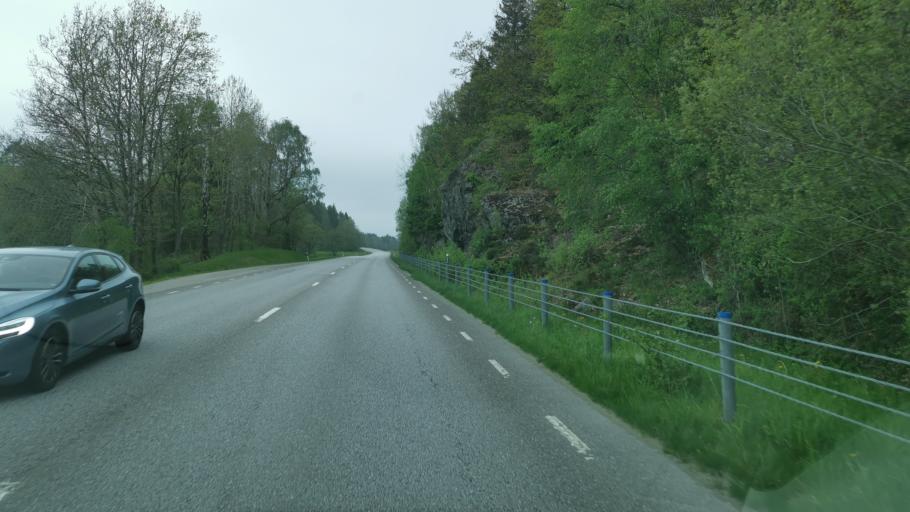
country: SE
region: Vaestra Goetaland
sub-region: Orust
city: Henan
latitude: 58.1841
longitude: 11.6938
